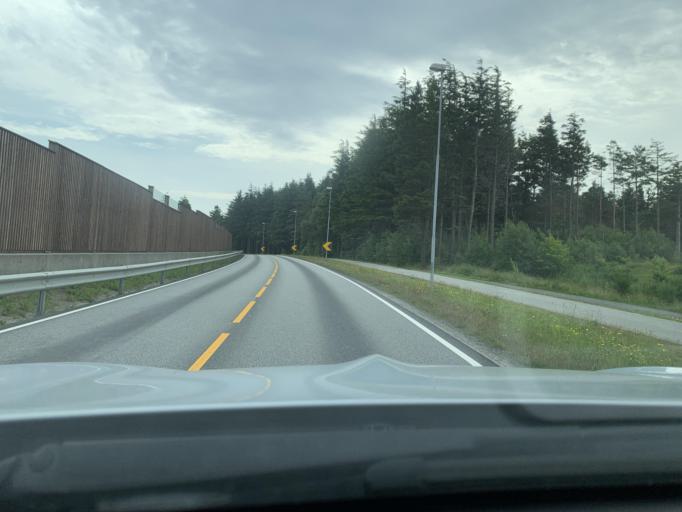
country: NO
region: Rogaland
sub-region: Sandnes
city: Sandnes
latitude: 58.7850
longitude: 5.7073
